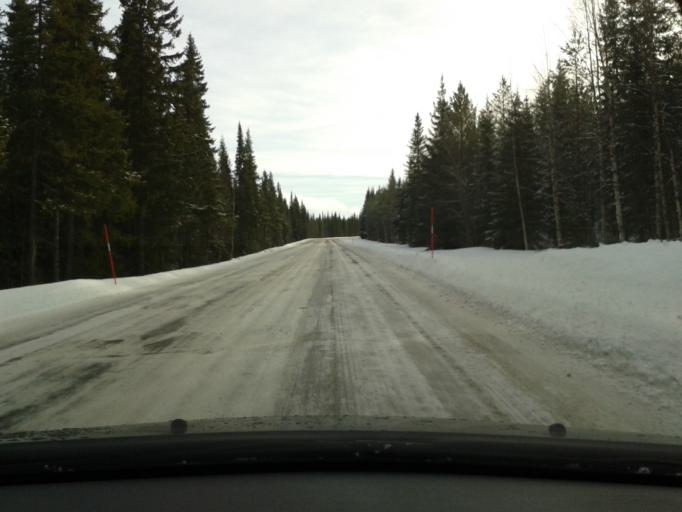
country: SE
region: Vaesterbotten
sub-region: Vilhelmina Kommun
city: Sjoberg
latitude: 64.7423
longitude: 16.2003
